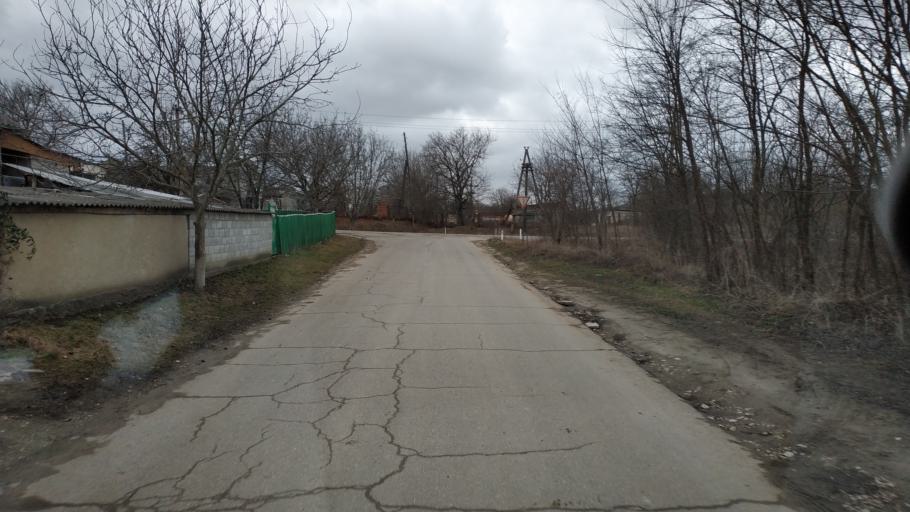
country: MD
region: Calarasi
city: Calarasi
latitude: 47.2459
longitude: 28.2869
